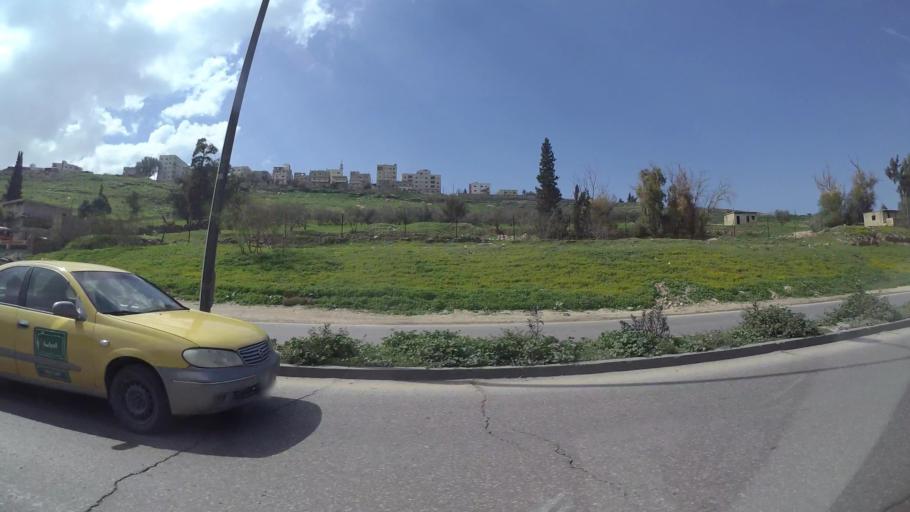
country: JO
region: Amman
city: Amman
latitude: 31.9857
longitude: 35.9767
